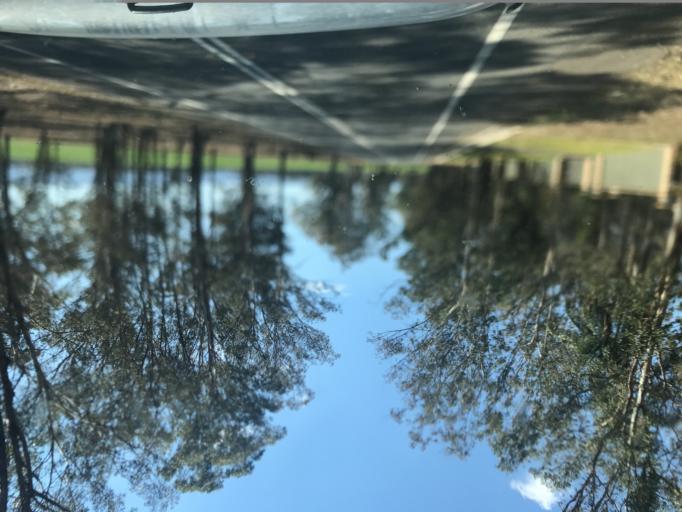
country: AU
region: New South Wales
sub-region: Hawkesbury
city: Richmond
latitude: -33.5651
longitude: 150.7508
